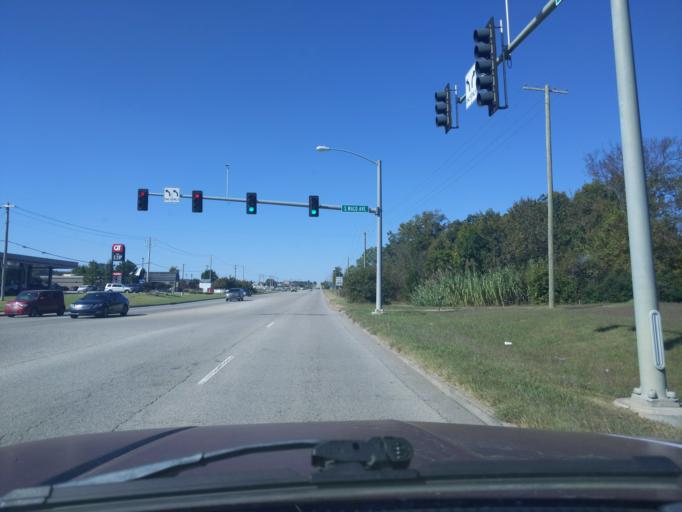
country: US
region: Oklahoma
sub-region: Tulsa County
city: Glenpool
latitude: 35.9884
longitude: -96.0162
